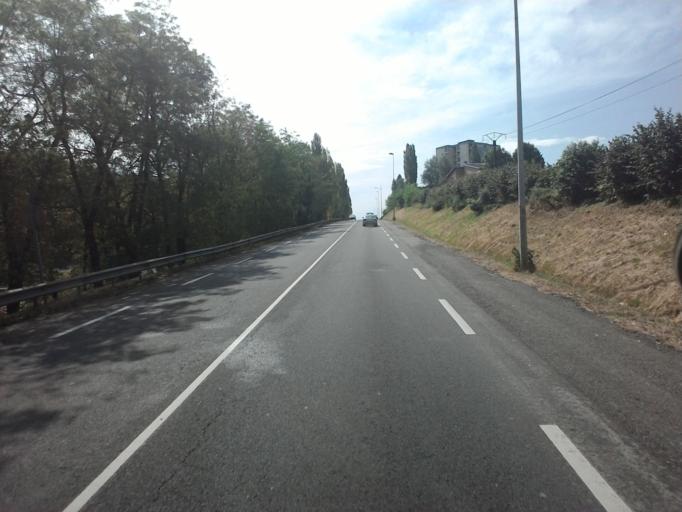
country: FR
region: Franche-Comte
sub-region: Departement du Jura
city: Perrigny
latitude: 46.6837
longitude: 5.5680
